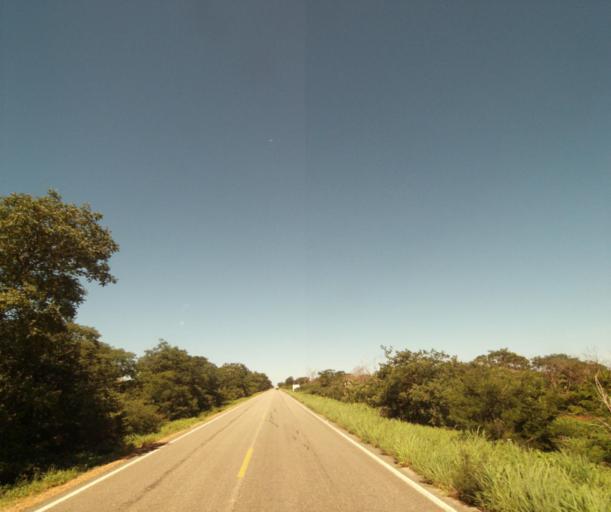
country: BR
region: Bahia
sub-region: Palmas De Monte Alto
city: Palmas de Monte Alto
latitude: -14.2641
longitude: -43.3407
